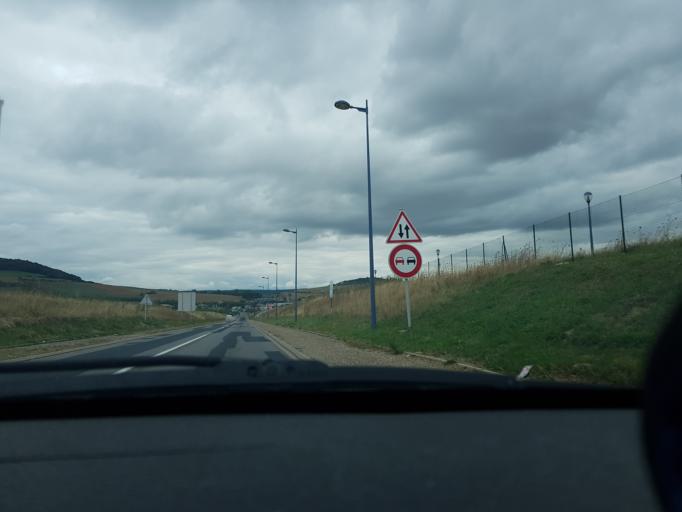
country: FR
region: Lorraine
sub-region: Departement de Meurthe-et-Moselle
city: Saulxures-les-Nancy
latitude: 48.6991
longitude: 6.2432
